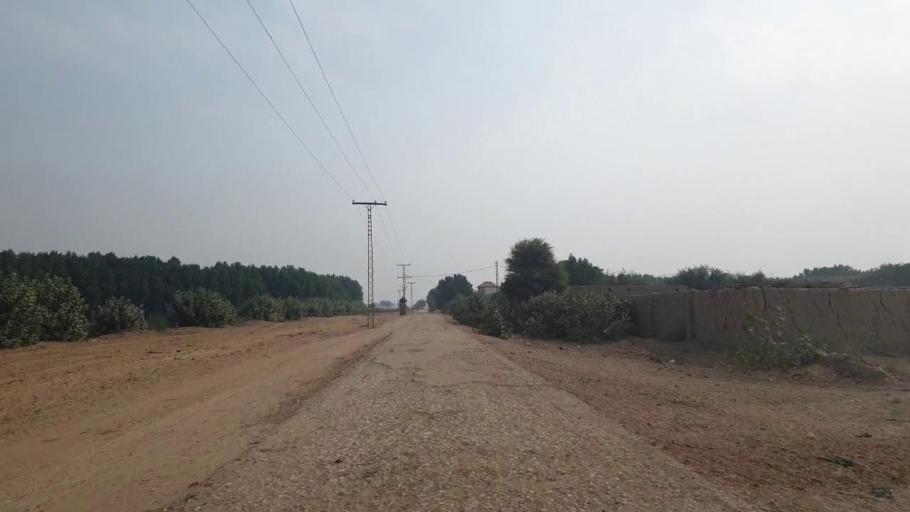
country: PK
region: Sindh
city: Sann
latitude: 26.0299
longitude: 68.1377
